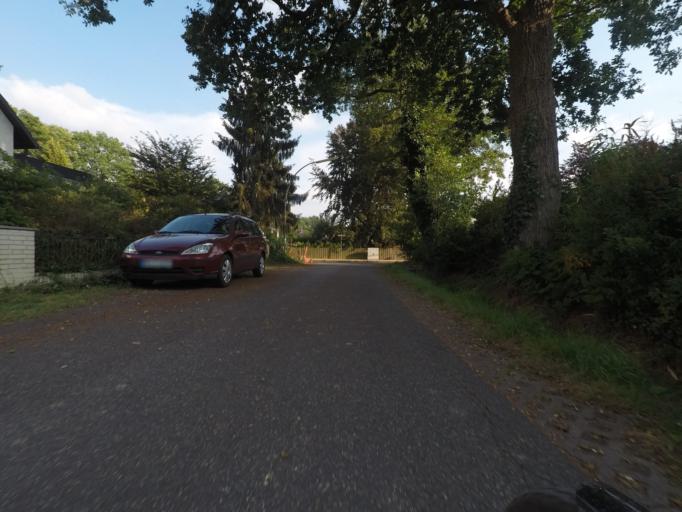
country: DE
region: Hamburg
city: Sasel
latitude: 53.6364
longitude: 10.1276
